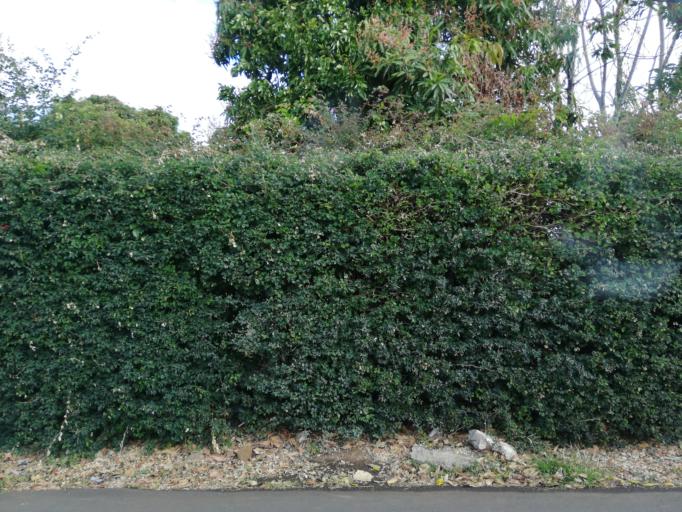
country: MU
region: Black River
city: Petite Riviere
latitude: -20.2253
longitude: 57.4620
